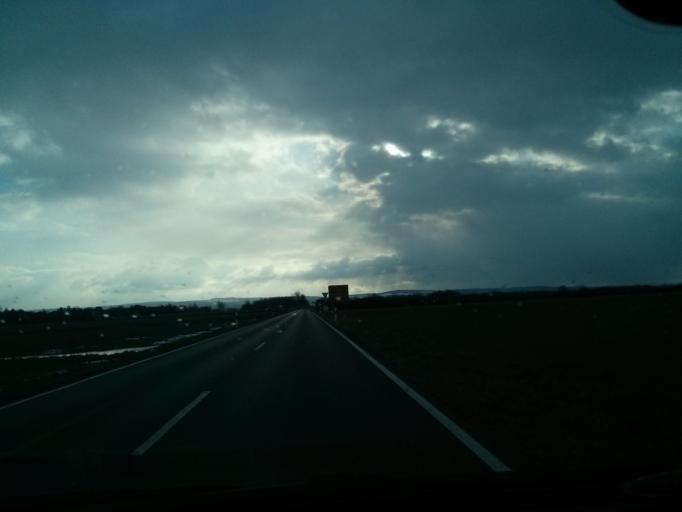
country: DE
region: North Rhine-Westphalia
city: Meckenheim
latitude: 50.6592
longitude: 7.0046
